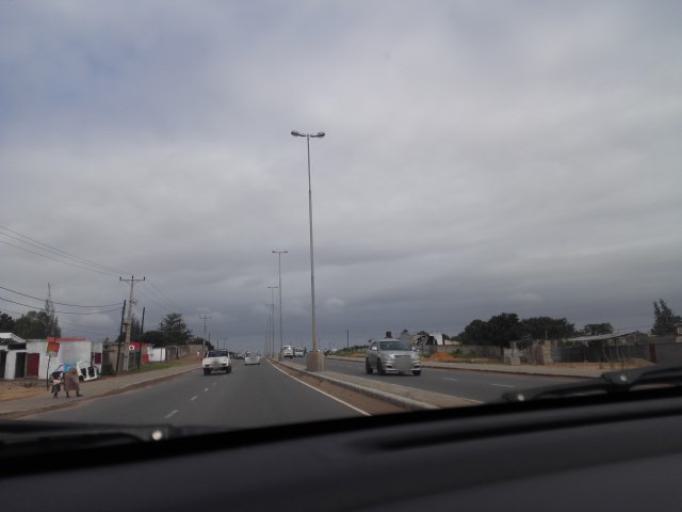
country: MZ
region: Maputo City
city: Maputo
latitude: -25.8254
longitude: 32.5981
